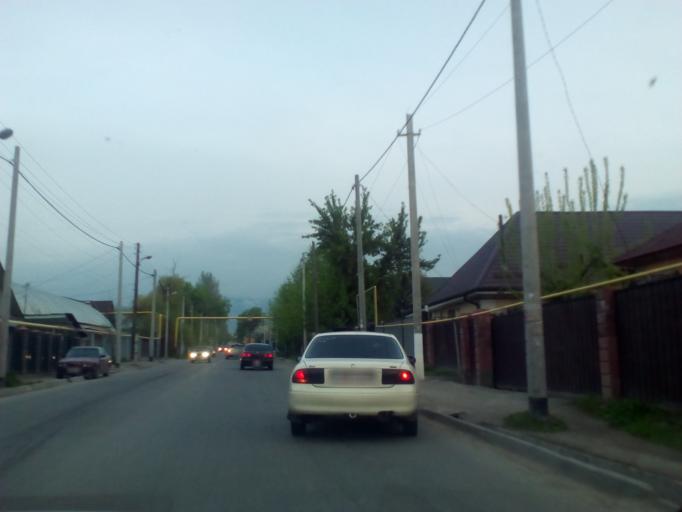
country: KZ
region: Almaty Qalasy
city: Almaty
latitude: 43.2324
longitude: 76.8259
